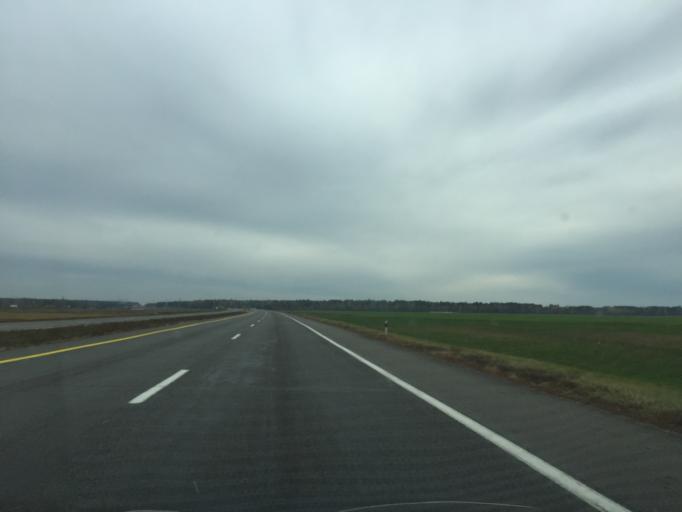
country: BY
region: Gomel
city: Horad Rechytsa
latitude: 52.3446
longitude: 30.5661
